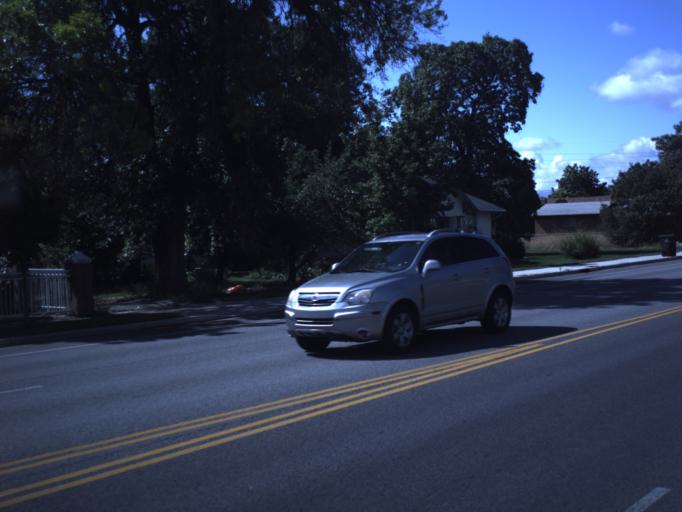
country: US
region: Utah
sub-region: Utah County
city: Springville
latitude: 40.1612
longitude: -111.6148
